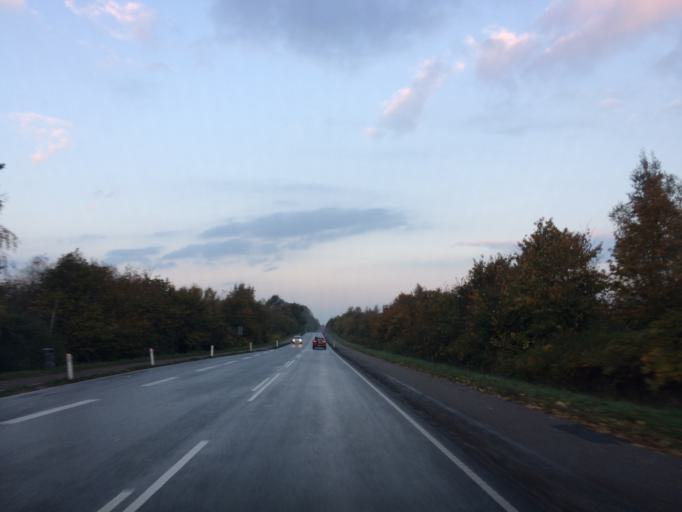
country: DK
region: Zealand
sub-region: Ringsted Kommune
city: Ringsted
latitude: 55.4655
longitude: 11.7617
